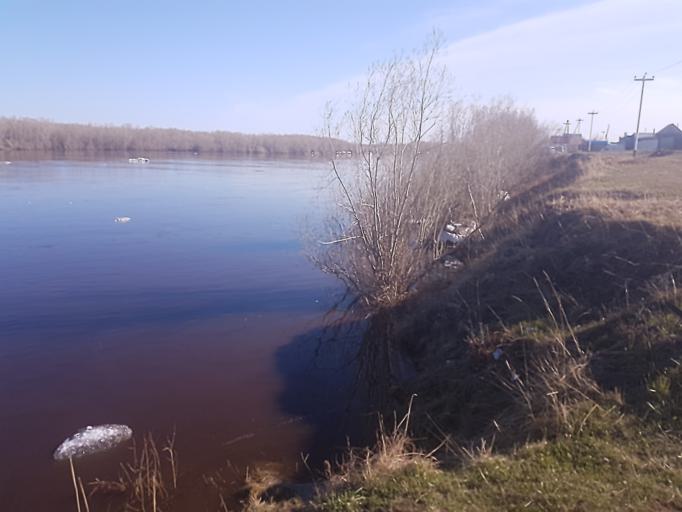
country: RU
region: Sakha
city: Yakutsk
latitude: 61.9726
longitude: 129.7008
